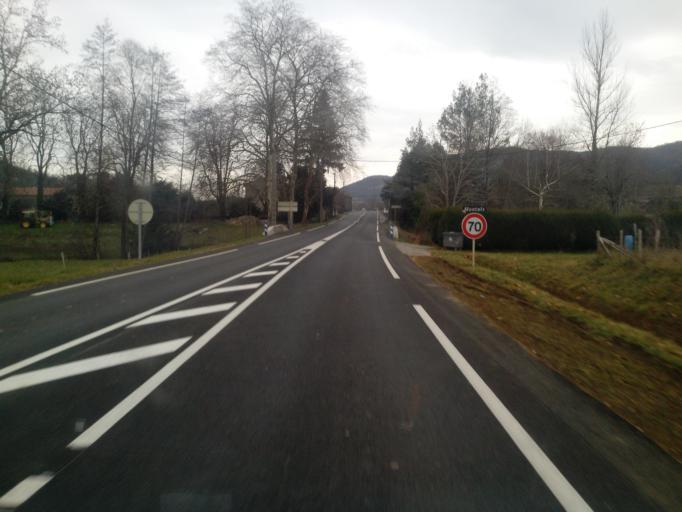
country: FR
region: Midi-Pyrenees
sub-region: Departement de l'Ariege
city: Foix
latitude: 43.0082
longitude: 1.4617
